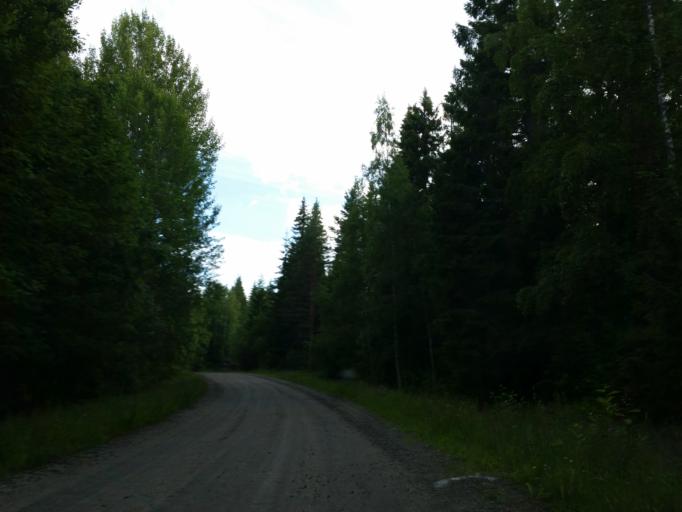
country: SE
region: Vaesterbotten
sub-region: Robertsfors Kommun
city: Robertsfors
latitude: 64.0459
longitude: 20.8507
